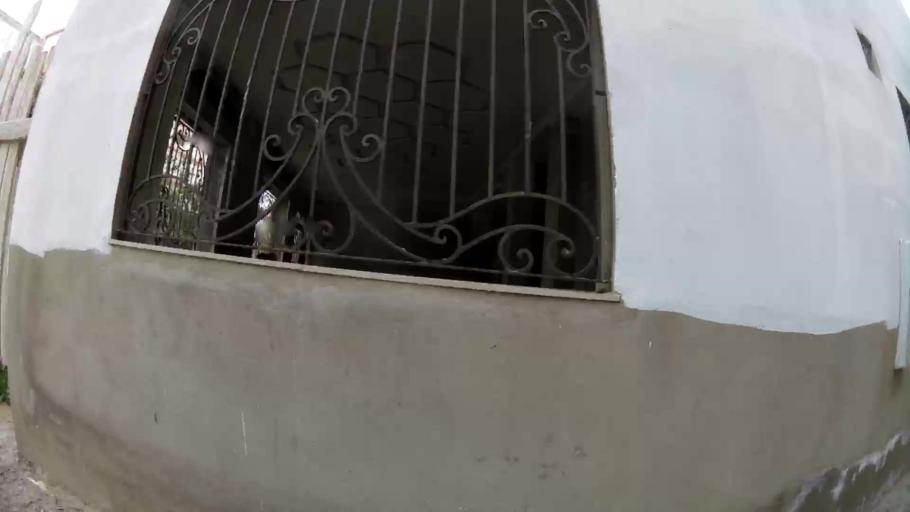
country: MA
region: Tanger-Tetouan
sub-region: Tanger-Assilah
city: Tangier
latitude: 35.7699
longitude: -5.7716
